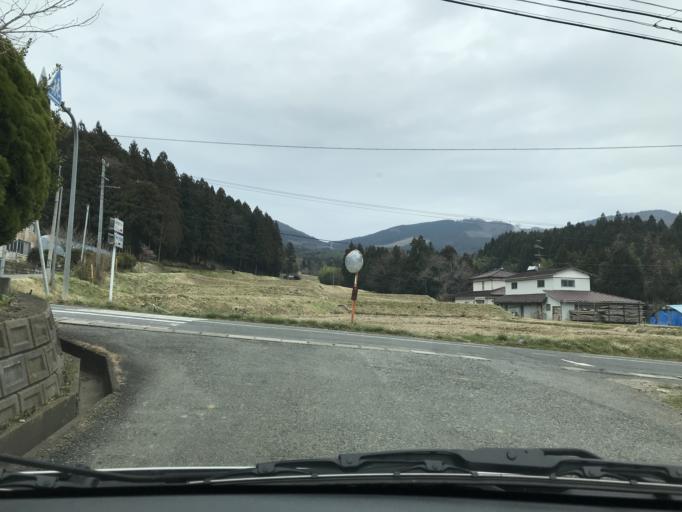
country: JP
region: Iwate
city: Mizusawa
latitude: 39.0438
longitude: 141.1616
